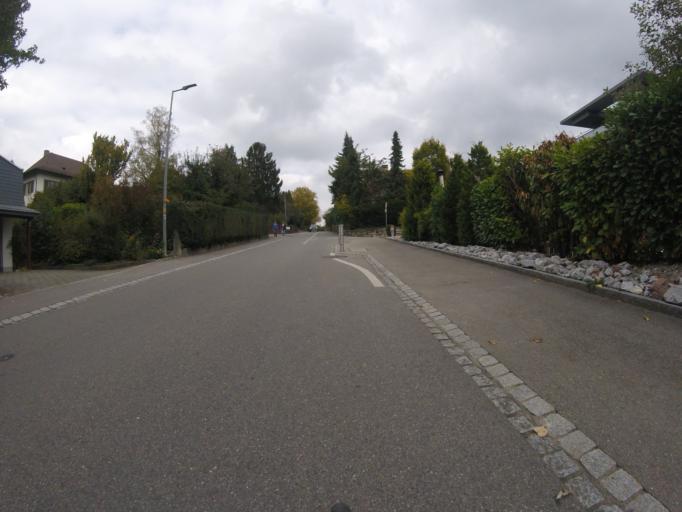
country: CH
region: Bern
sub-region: Bern-Mittelland District
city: Munsingen
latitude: 46.8793
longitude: 7.5625
